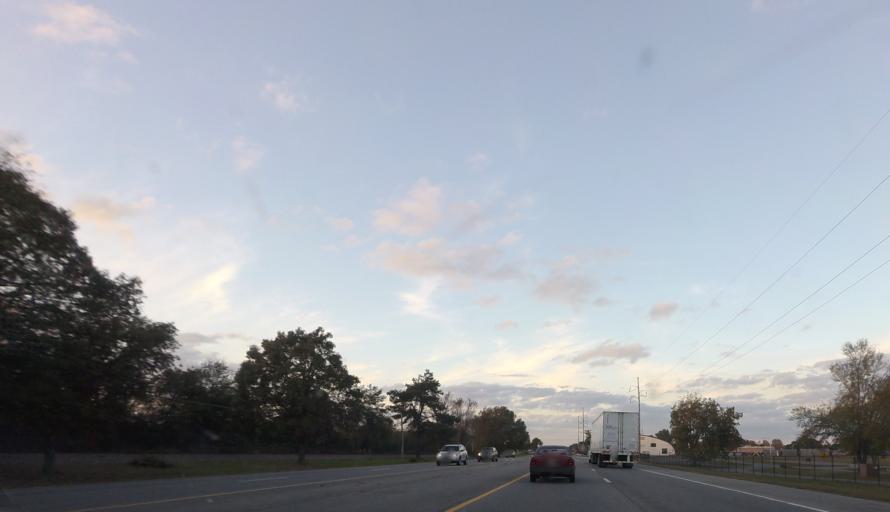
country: US
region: Georgia
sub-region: Houston County
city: Robins Air Force Base
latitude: 32.6026
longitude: -83.5938
